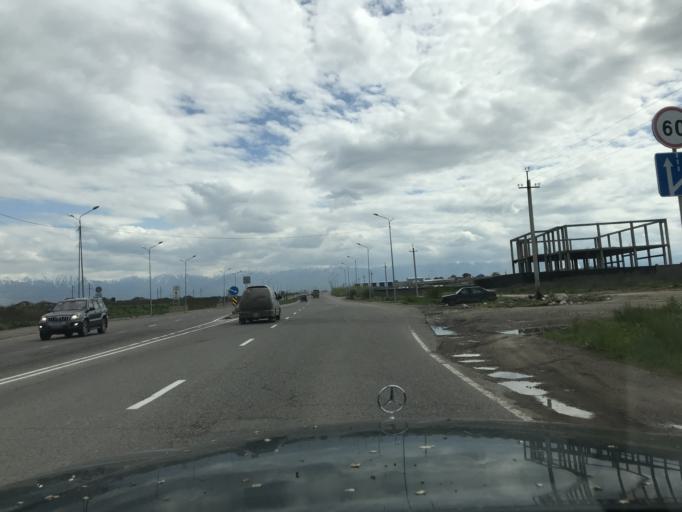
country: KZ
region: Almaty Oblysy
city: Burunday
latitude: 43.3483
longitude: 76.8337
